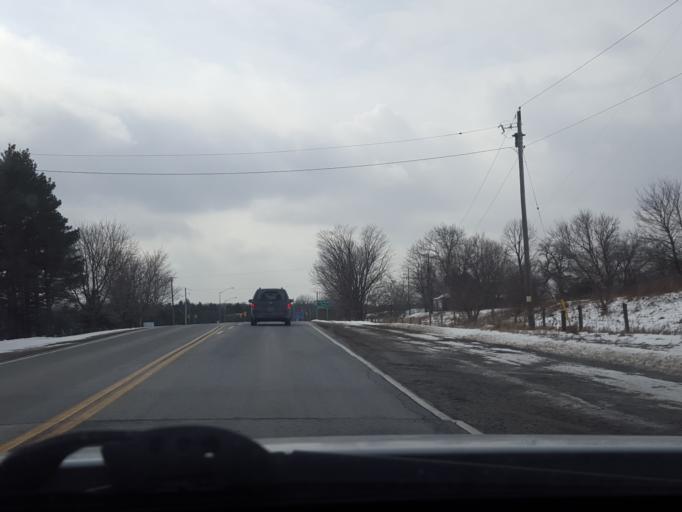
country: CA
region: Ontario
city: Uxbridge
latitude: 44.0600
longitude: -79.0648
